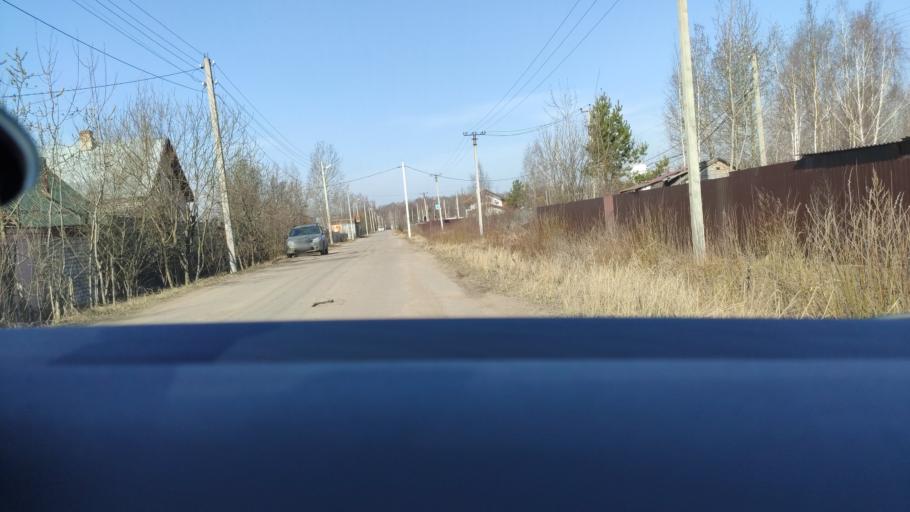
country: RU
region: Moskovskaya
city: Imeni Vorovskogo
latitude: 55.7793
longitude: 38.3684
